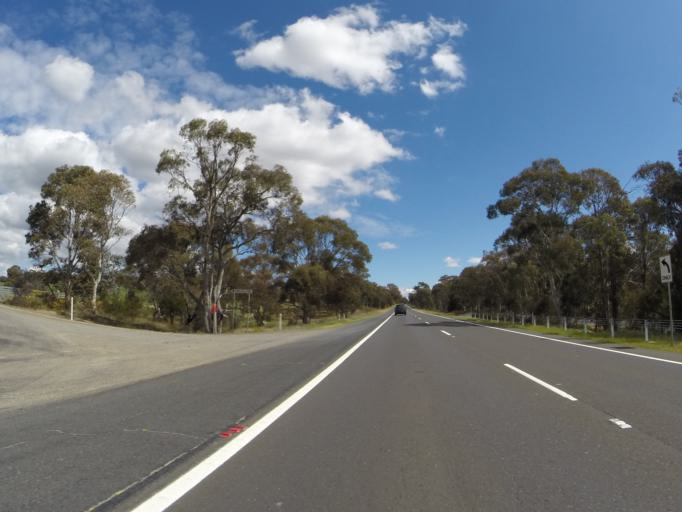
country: AU
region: New South Wales
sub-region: Goulburn Mulwaree
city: Goulburn
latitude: -34.7455
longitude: 149.8732
